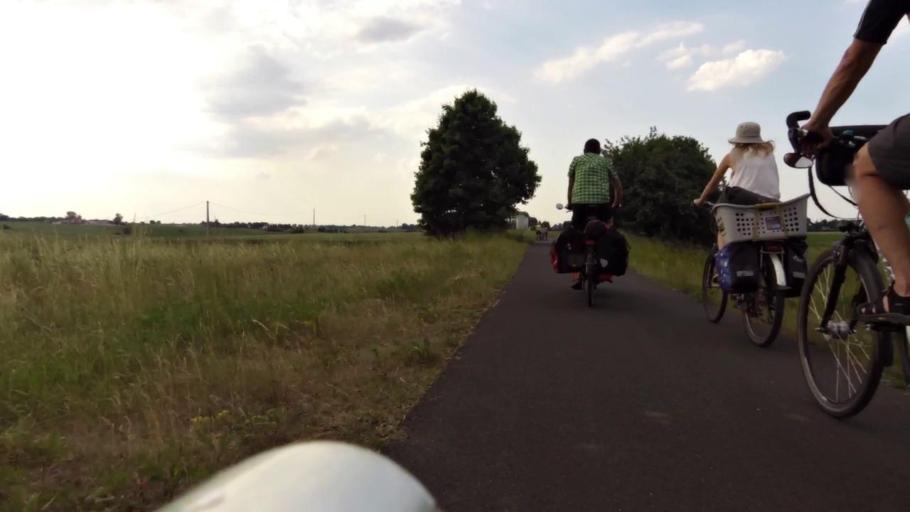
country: PL
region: Kujawsko-Pomorskie
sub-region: Powiat torunski
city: Lubianka
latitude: 53.1263
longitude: 18.4669
